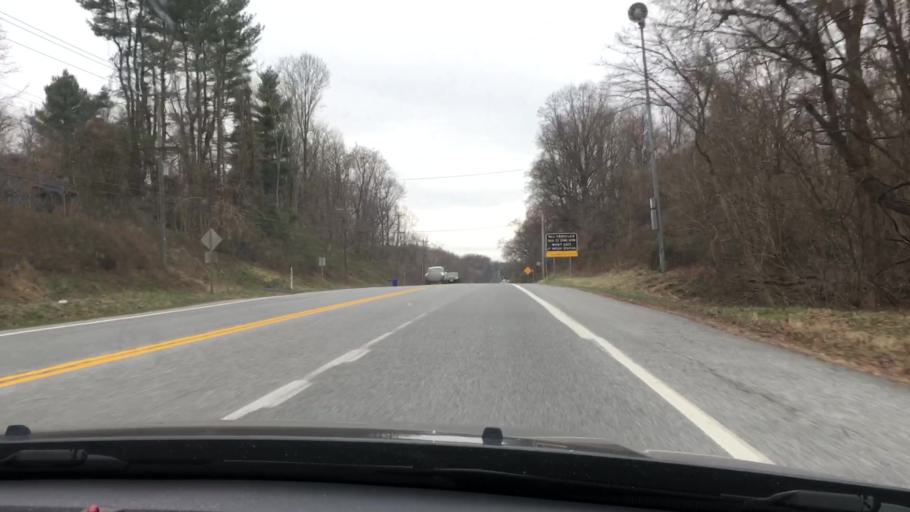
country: US
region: Maryland
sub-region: Cecil County
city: Rising Sun
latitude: 39.6522
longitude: -76.1905
